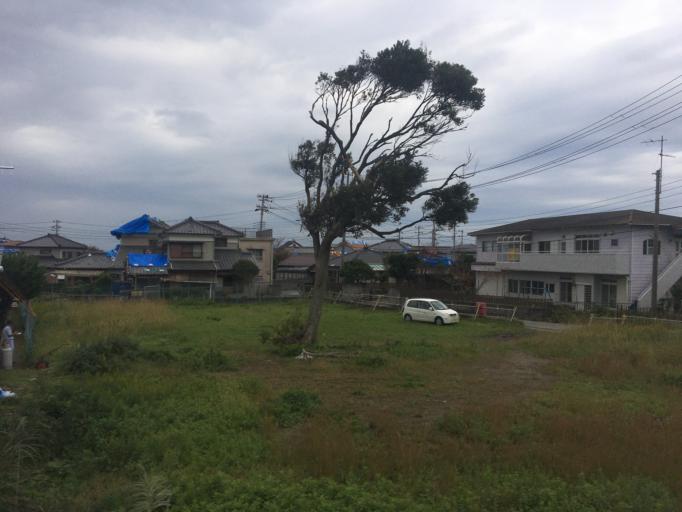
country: JP
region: Chiba
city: Tateyama
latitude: 35.1355
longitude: 139.8398
